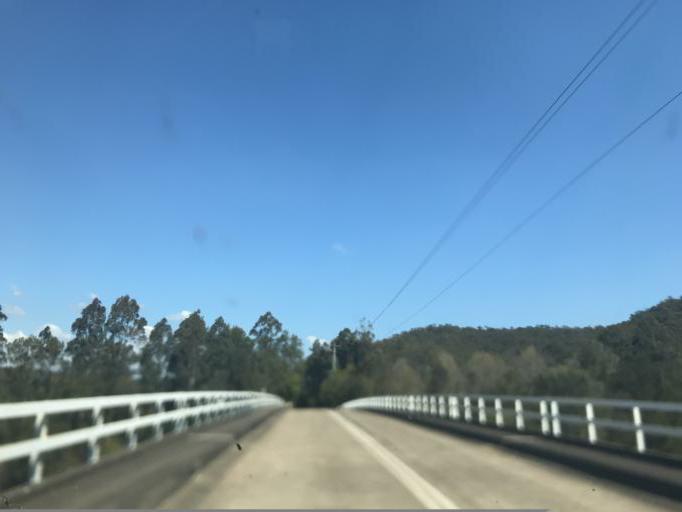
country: AU
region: New South Wales
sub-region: Hawkesbury
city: Pitt Town
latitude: -33.4364
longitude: 150.8835
